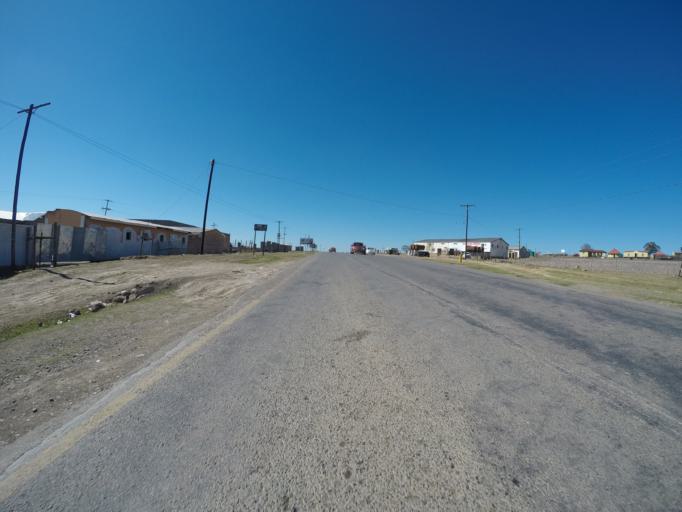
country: ZA
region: Eastern Cape
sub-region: OR Tambo District Municipality
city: Mthatha
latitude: -31.8750
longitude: 28.7537
